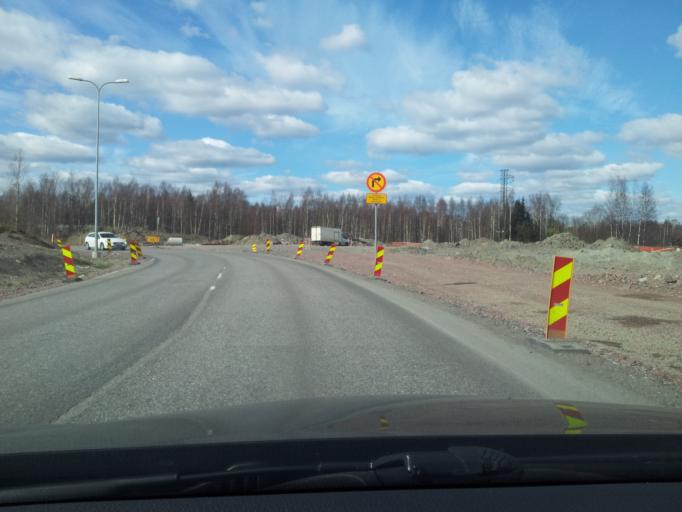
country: FI
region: Uusimaa
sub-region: Helsinki
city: Kilo
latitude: 60.1846
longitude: 24.7762
